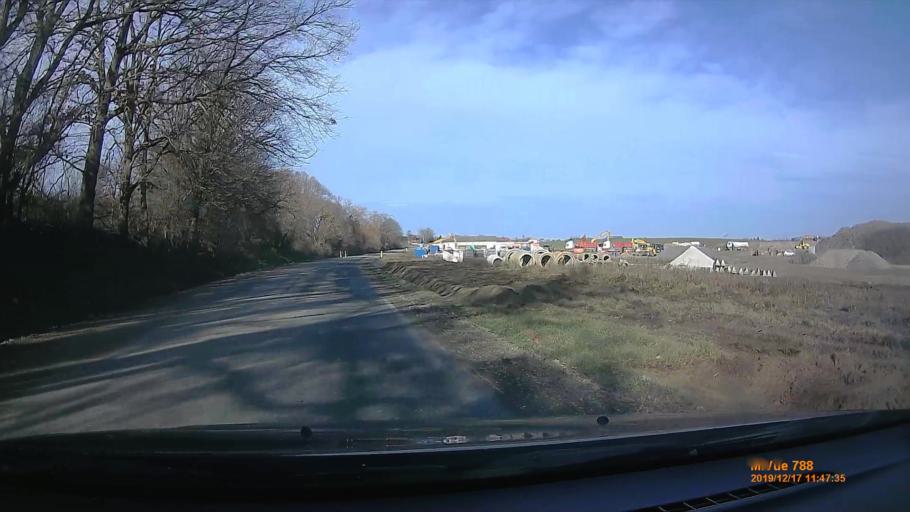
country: HU
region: Somogy
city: Kaposvar
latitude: 46.4462
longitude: 17.7674
